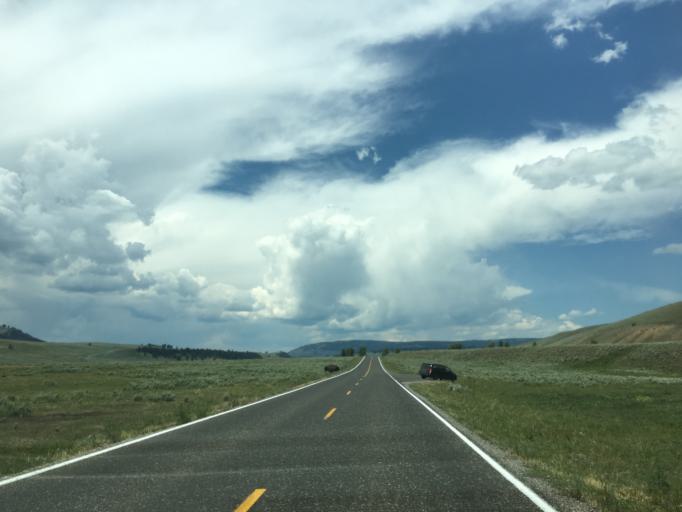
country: US
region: Montana
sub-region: Park County
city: Livingston
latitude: 44.8907
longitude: -110.2284
